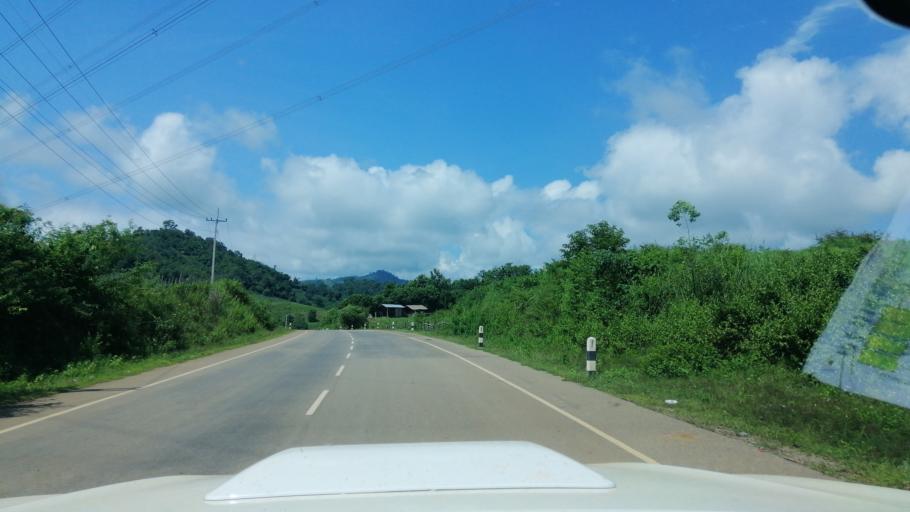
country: TH
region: Uttaradit
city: Ban Khok
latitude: 18.1362
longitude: 101.3724
